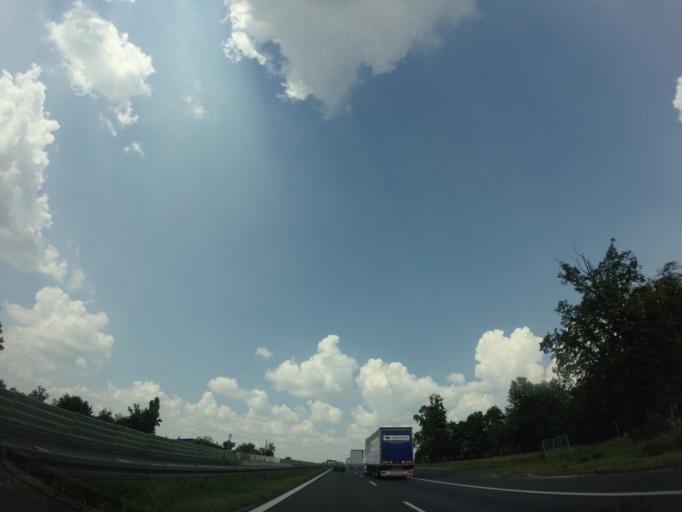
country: PL
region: Silesian Voivodeship
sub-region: Powiat gliwicki
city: Rudziniec
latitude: 50.4118
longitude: 18.4097
